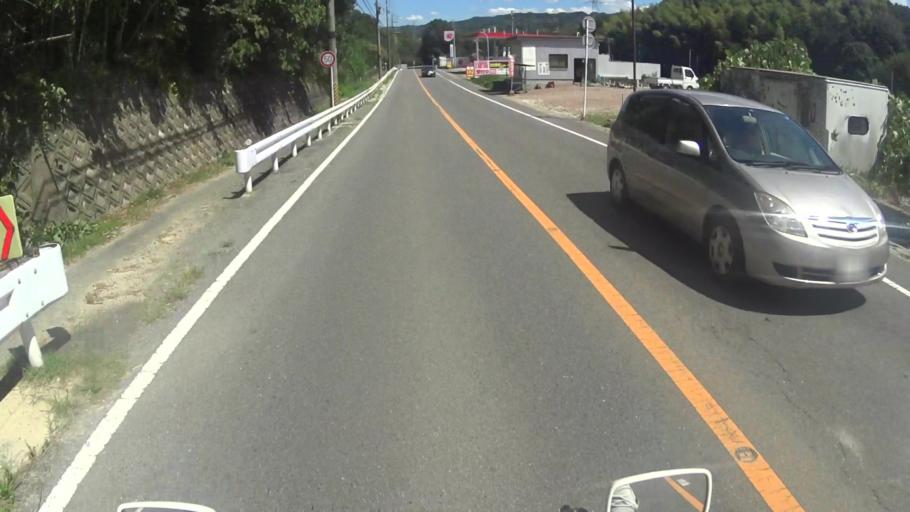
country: JP
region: Nara
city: Nara-shi
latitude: 34.7303
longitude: 135.8597
